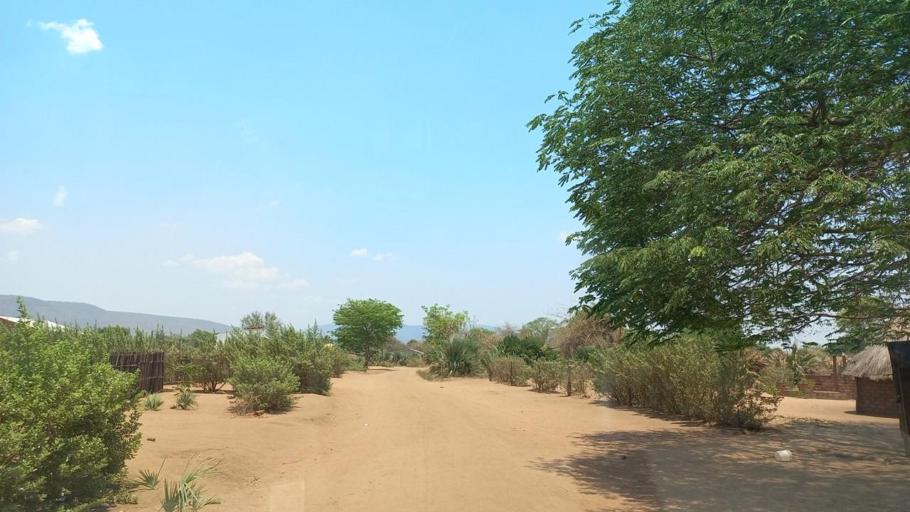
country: ZM
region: Lusaka
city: Luangwa
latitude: -15.1923
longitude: 30.1858
